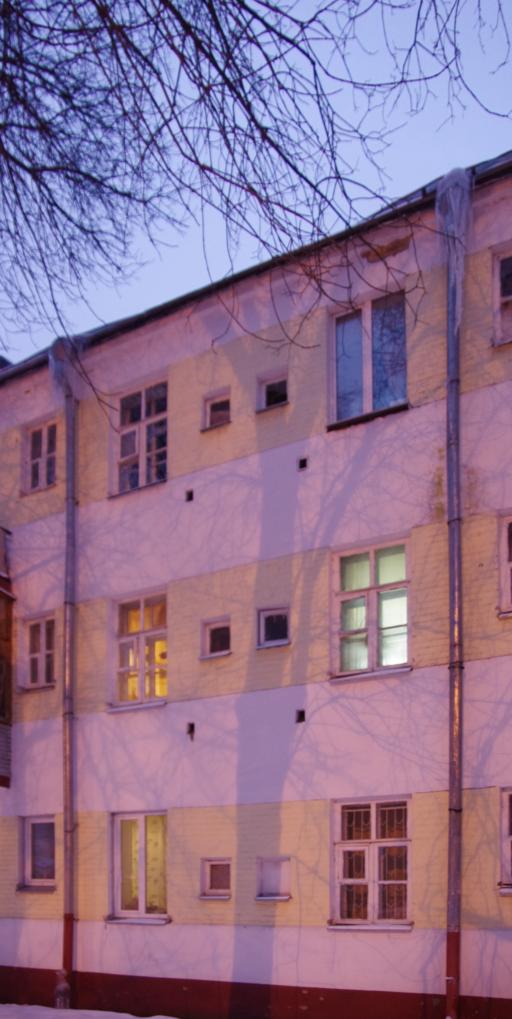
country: RU
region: Moskovskaya
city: Korolev
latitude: 55.9222
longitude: 37.8091
